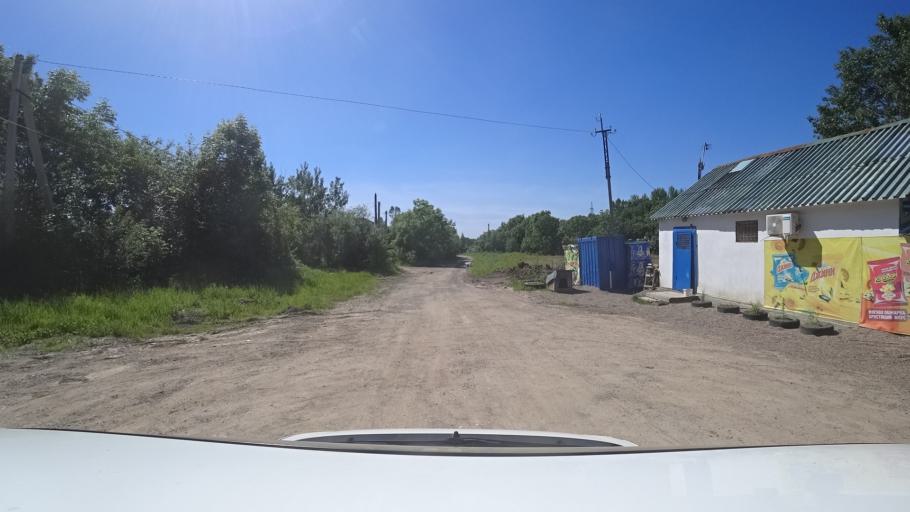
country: RU
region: Khabarovsk Krai
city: Topolevo
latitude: 48.5589
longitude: 135.1923
